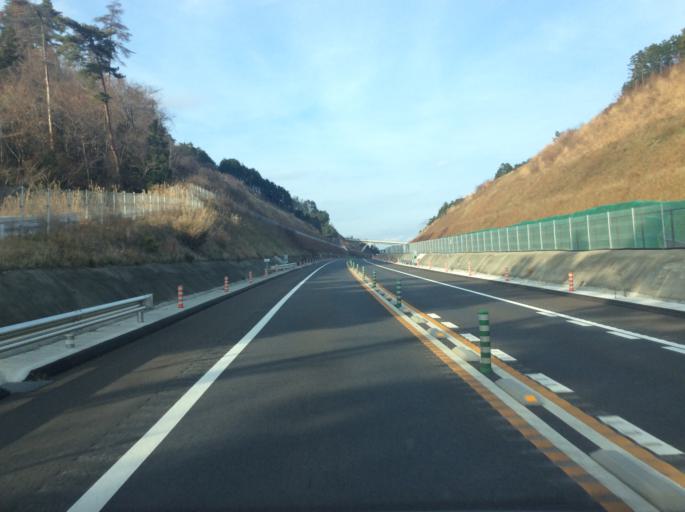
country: JP
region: Fukushima
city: Namie
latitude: 37.4366
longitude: 140.9584
